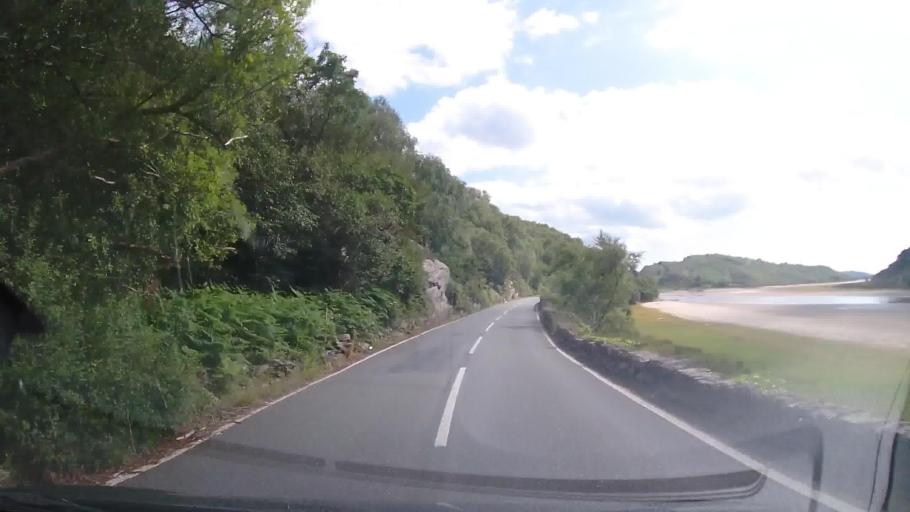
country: GB
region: Wales
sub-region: Gwynedd
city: Penrhyndeudraeth
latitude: 52.9317
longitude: -4.0411
